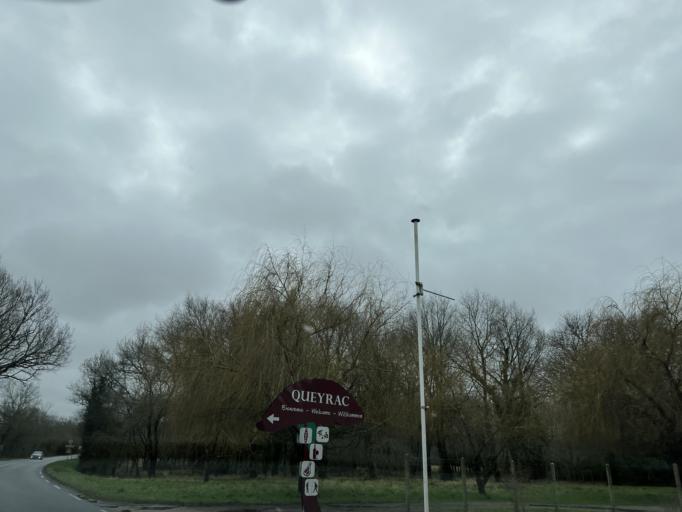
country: FR
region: Aquitaine
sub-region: Departement de la Gironde
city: Gaillan-en-Medoc
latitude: 45.3492
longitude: -0.9886
